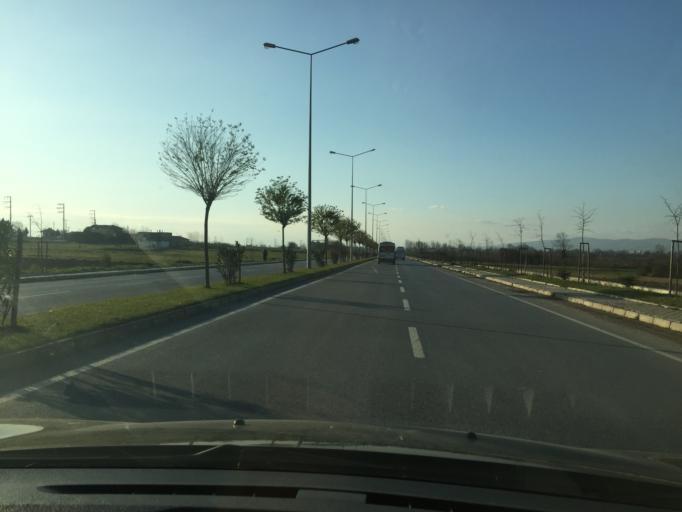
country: TR
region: Sakarya
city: Sogutlu
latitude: 40.9027
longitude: 30.4989
